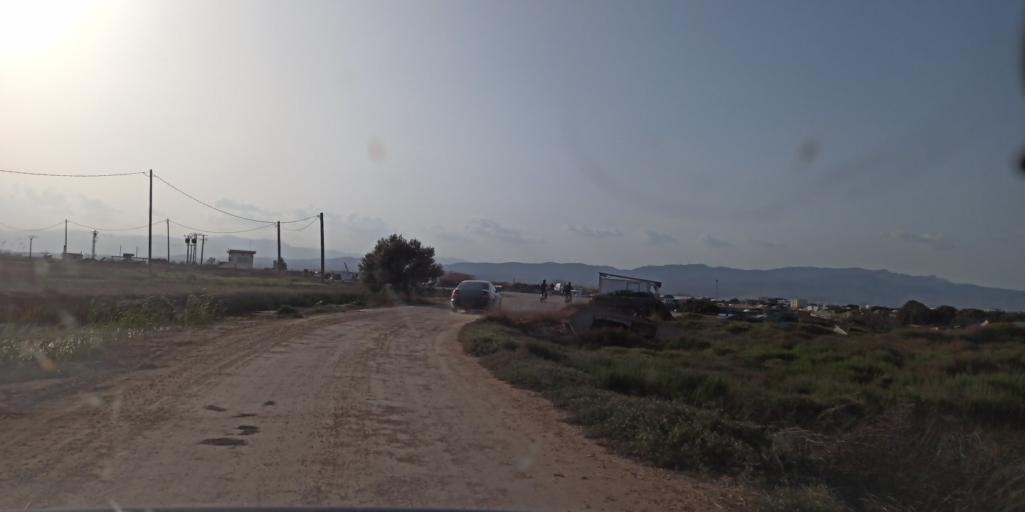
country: ES
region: Catalonia
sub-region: Provincia de Tarragona
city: L'Ampolla
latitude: 40.7662
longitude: 0.7401
